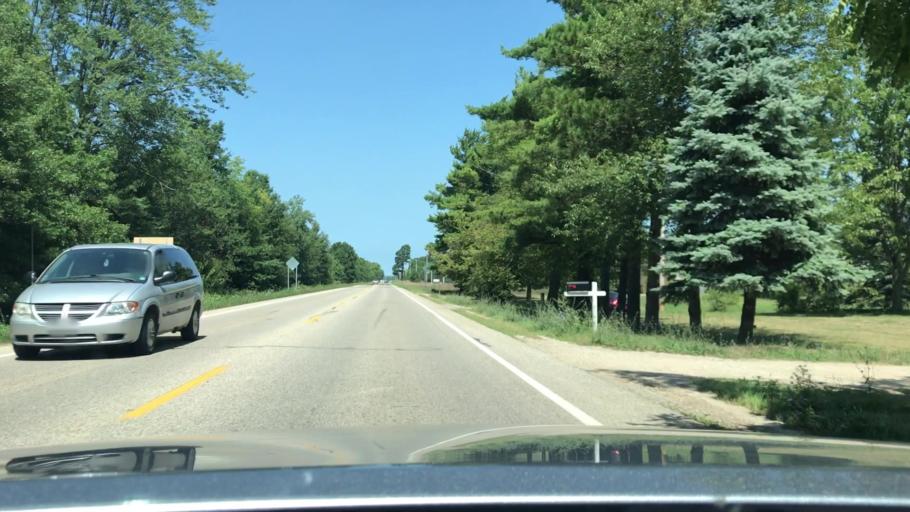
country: US
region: Michigan
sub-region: Ottawa County
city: Allendale
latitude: 42.9437
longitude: -86.0821
